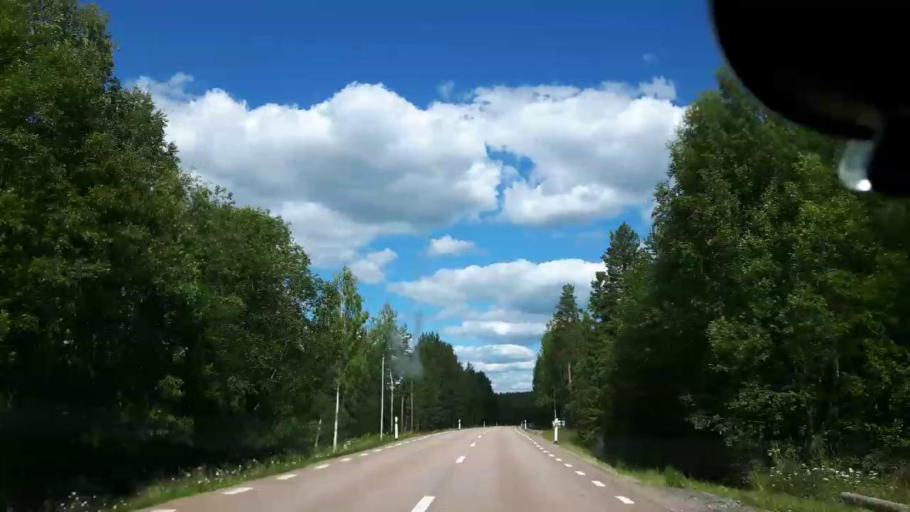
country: SE
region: Jaemtland
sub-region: Ragunda Kommun
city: Hammarstrand
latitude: 62.9124
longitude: 16.7025
